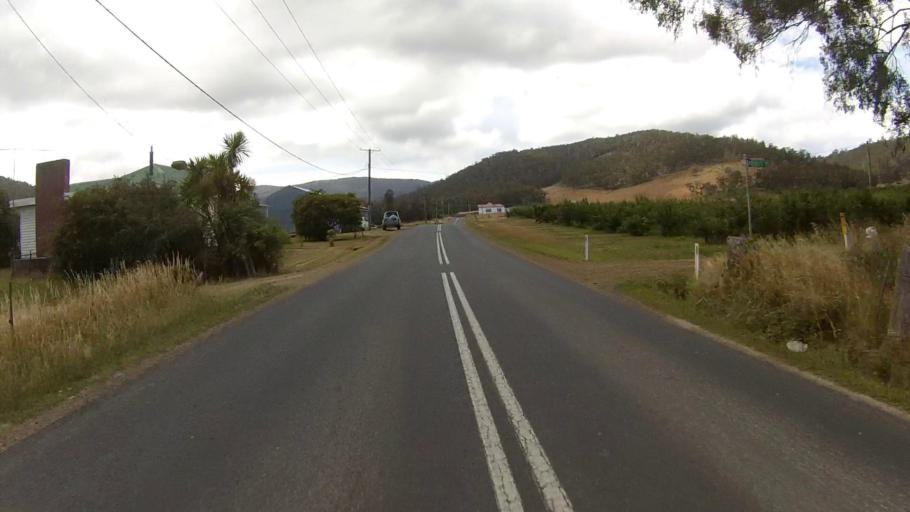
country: AU
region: Tasmania
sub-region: Huon Valley
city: Cygnet
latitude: -43.1653
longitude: 147.1277
